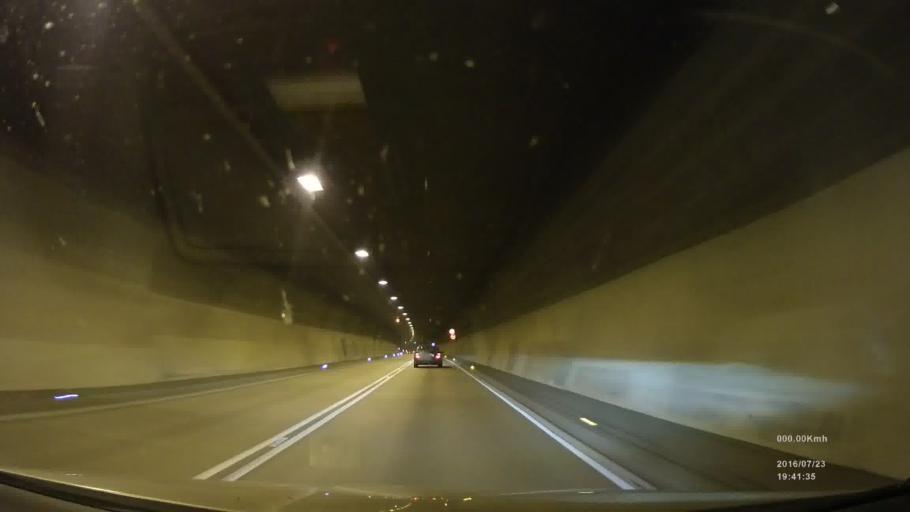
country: SK
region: Kosicky
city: Krompachy
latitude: 48.9974
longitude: 20.9017
